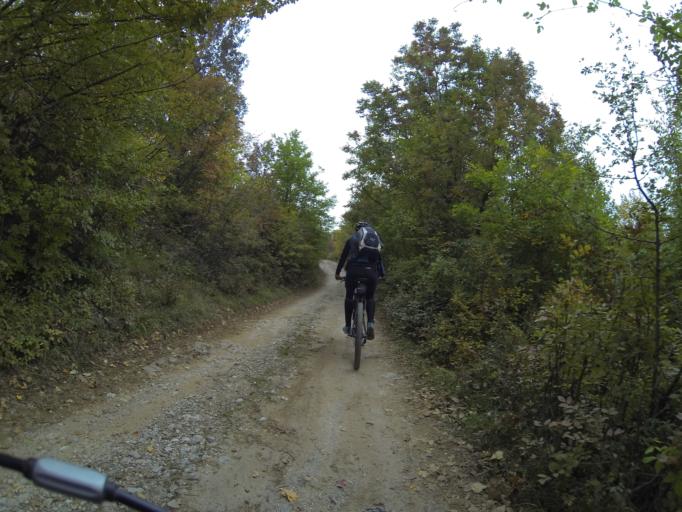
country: RO
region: Gorj
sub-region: Comuna Tismana
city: Sohodol
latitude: 45.0647
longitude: 22.8680
